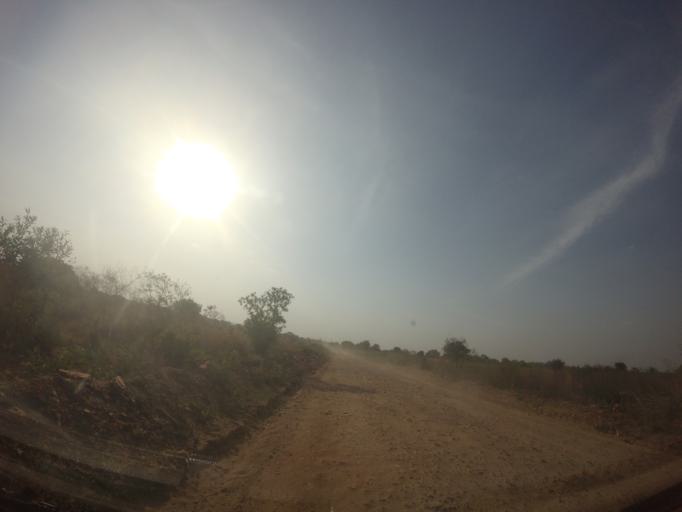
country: UG
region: Northern Region
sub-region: Maracha District
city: Maracha
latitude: 3.1140
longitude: 31.1355
